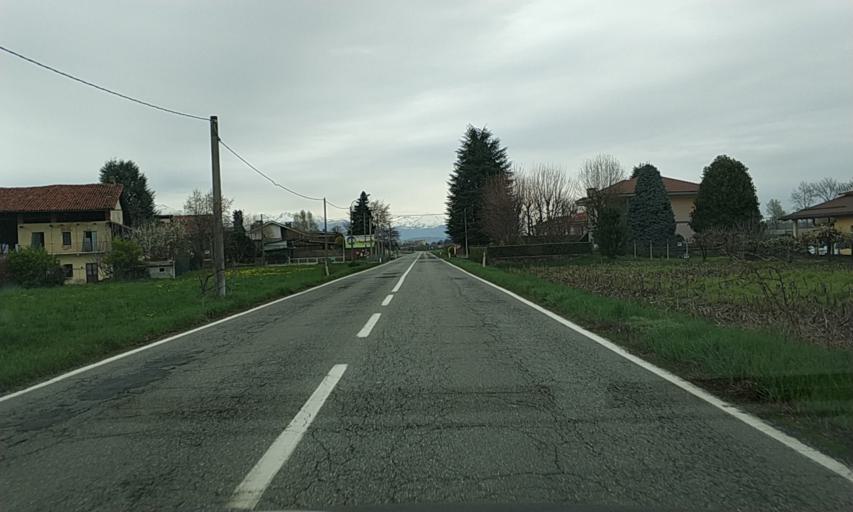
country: IT
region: Piedmont
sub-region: Provincia di Torino
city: Favria
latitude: 45.3160
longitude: 7.6801
